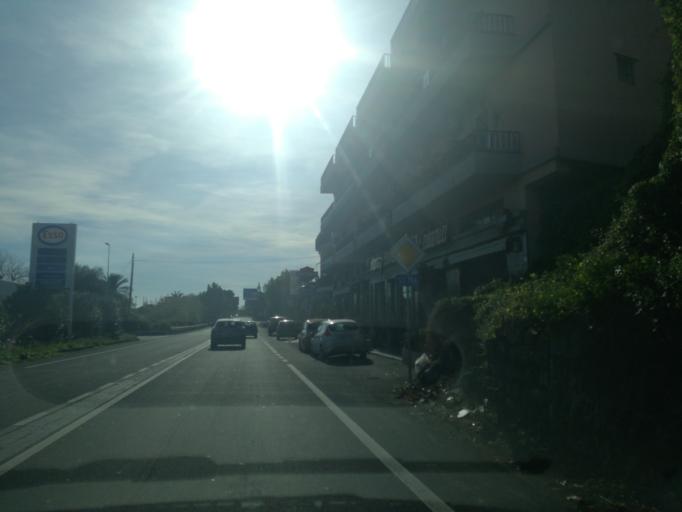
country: IT
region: Sicily
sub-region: Catania
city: Acireale
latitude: 37.6018
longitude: 15.1682
